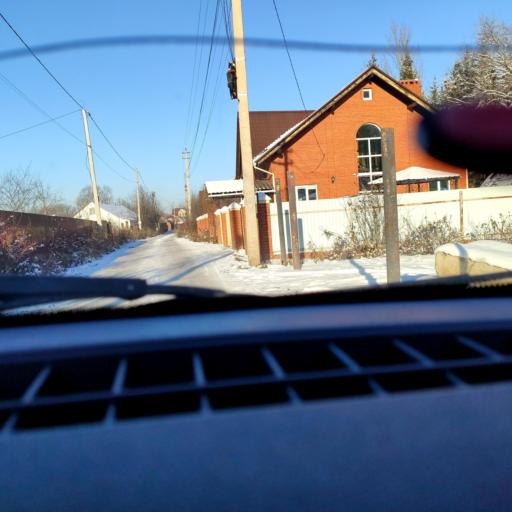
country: RU
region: Bashkortostan
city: Ufa
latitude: 54.6555
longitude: 55.9258
